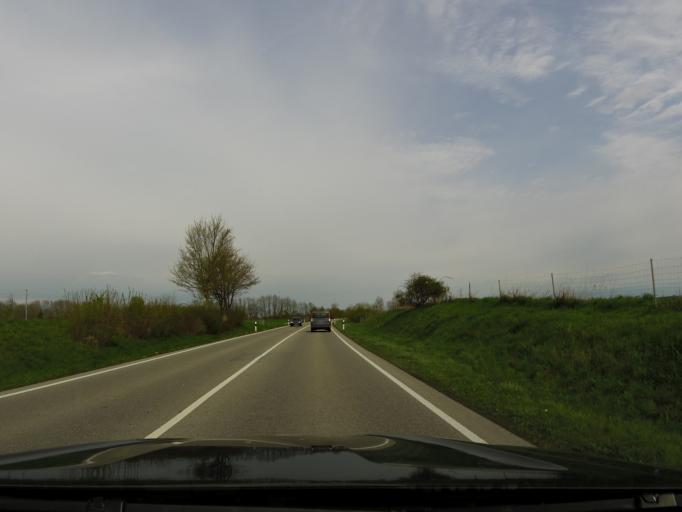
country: DE
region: Bavaria
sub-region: Upper Bavaria
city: Oberding
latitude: 48.3448
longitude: 11.8549
